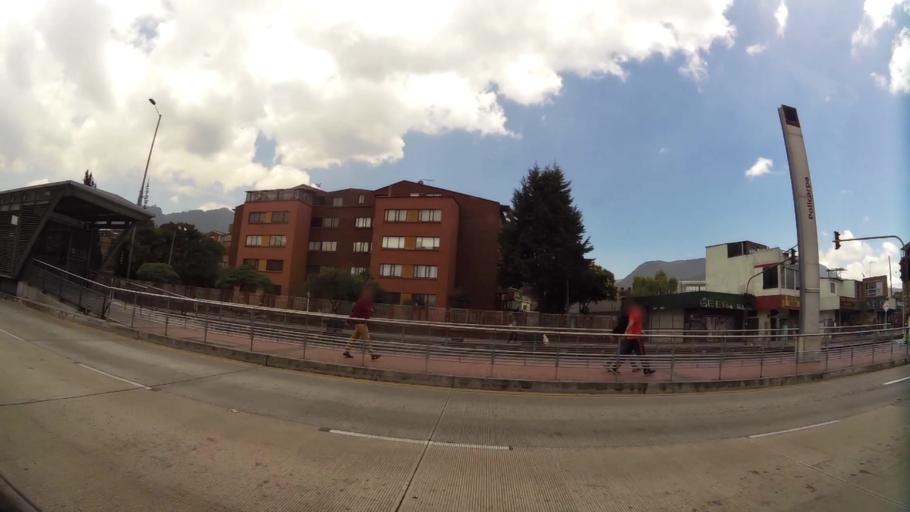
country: CO
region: Bogota D.C.
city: Bogota
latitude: 4.5828
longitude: -74.0858
